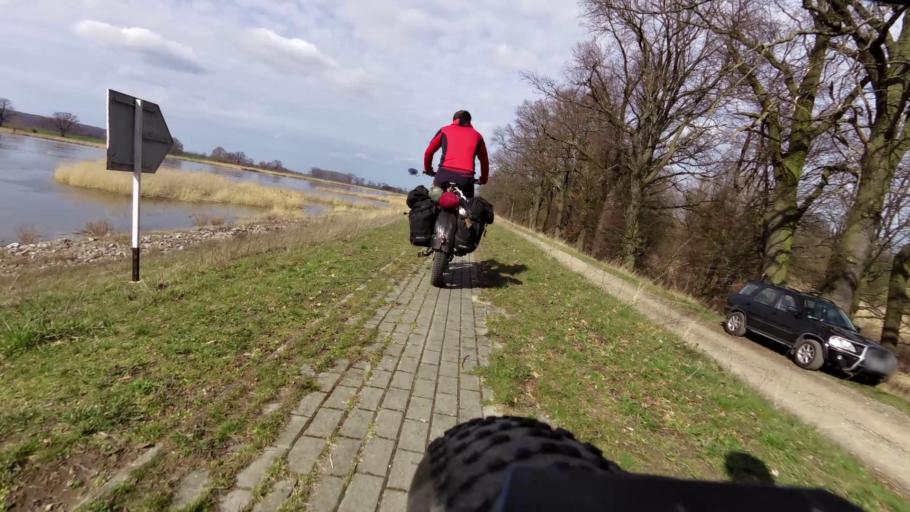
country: DE
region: Brandenburg
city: Reitwein
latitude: 52.4682
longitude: 14.6136
